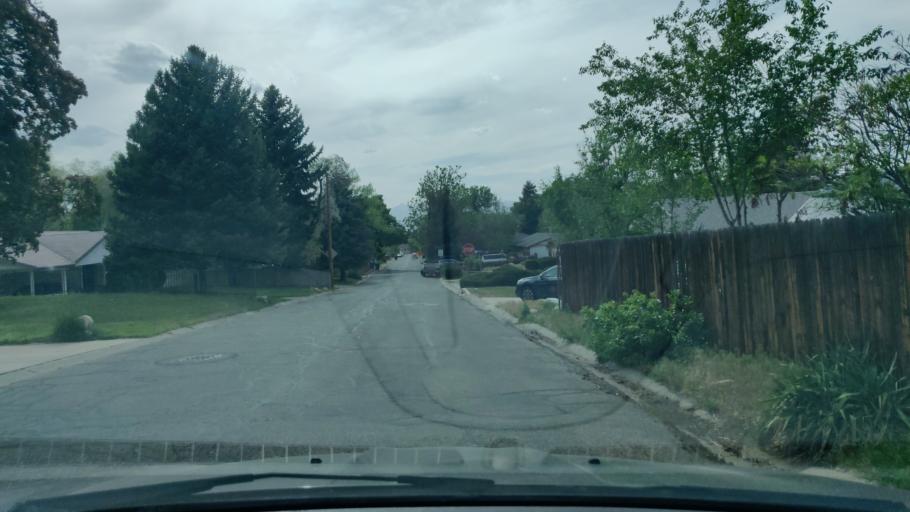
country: US
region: Utah
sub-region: Salt Lake County
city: Cottonwood Heights
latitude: 40.6172
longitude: -111.8080
